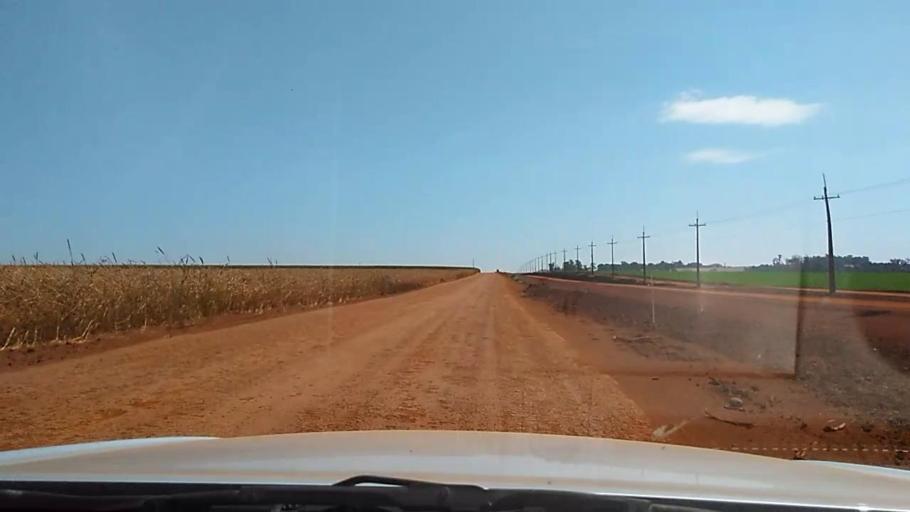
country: PY
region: Alto Parana
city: Naranjal
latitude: -25.9732
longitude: -55.2334
